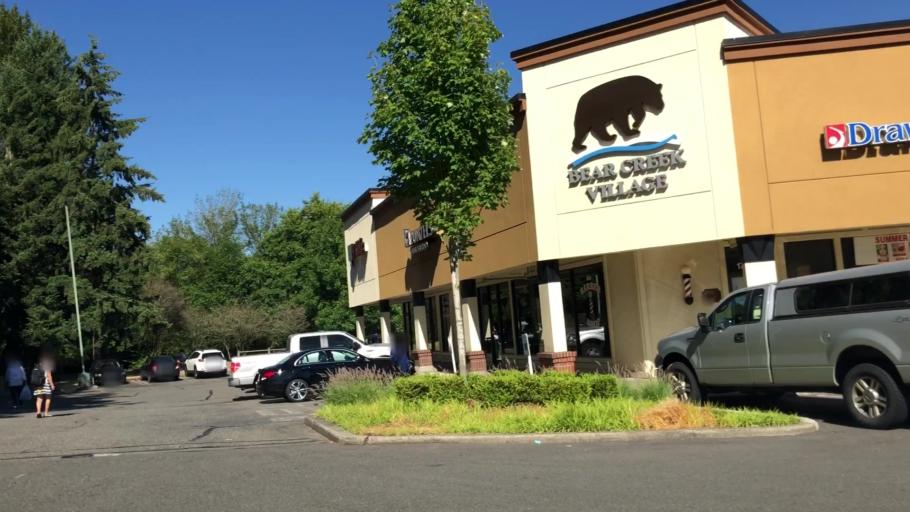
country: US
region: Washington
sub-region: King County
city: Redmond
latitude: 47.6728
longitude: -122.1103
